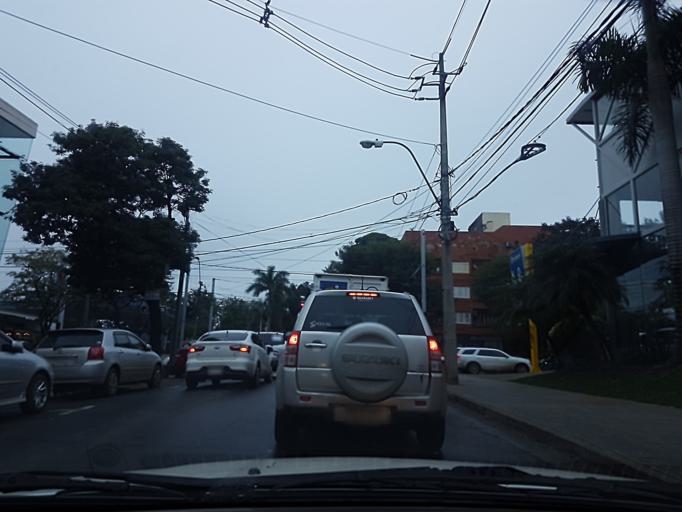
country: PY
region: Central
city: Fernando de la Mora
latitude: -25.2998
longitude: -57.5663
